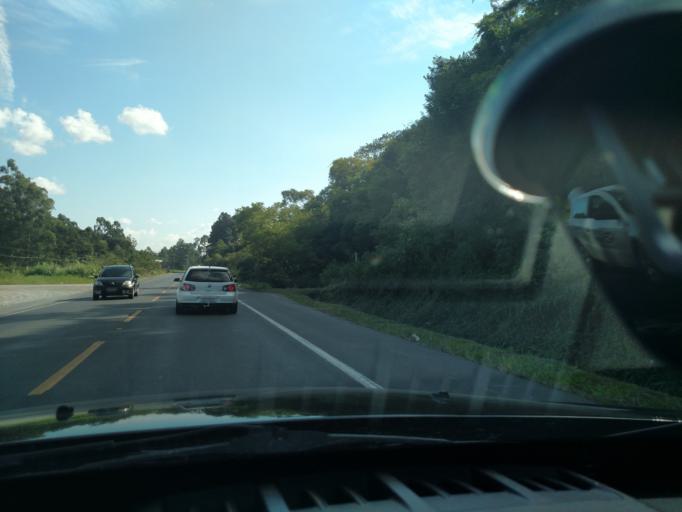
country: BR
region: Santa Catarina
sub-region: Rio Do Sul
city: Rio do Sul
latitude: -27.2293
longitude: -49.6689
